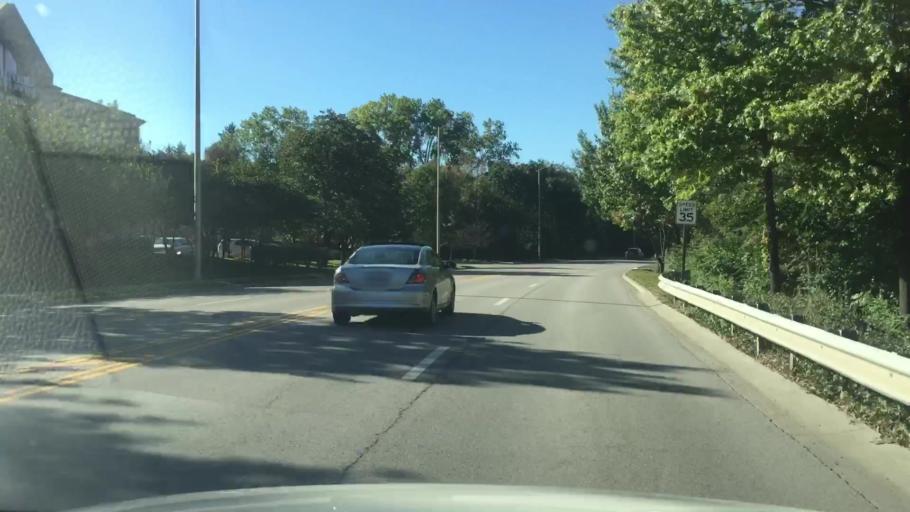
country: US
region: Kansas
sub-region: Johnson County
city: Leawood
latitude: 38.9287
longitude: -94.6264
